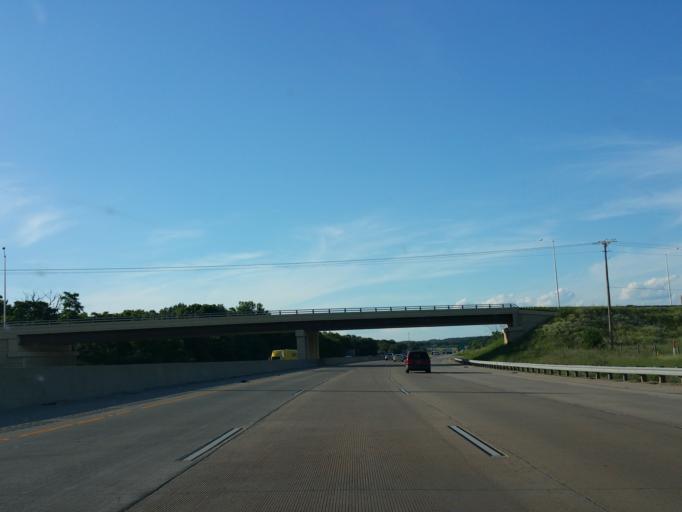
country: US
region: Wisconsin
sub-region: Columbia County
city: Poynette
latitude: 43.3909
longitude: -89.4666
